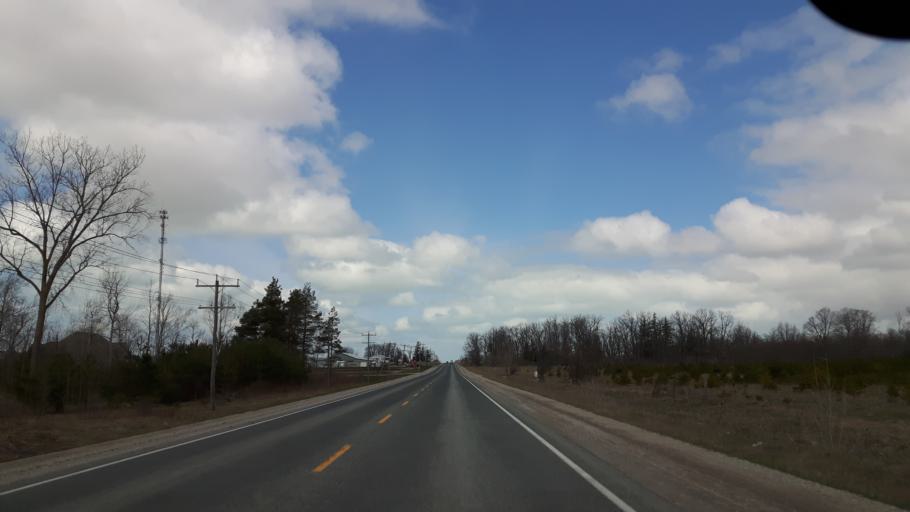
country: CA
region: Ontario
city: Goderich
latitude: 43.7153
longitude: -81.6674
